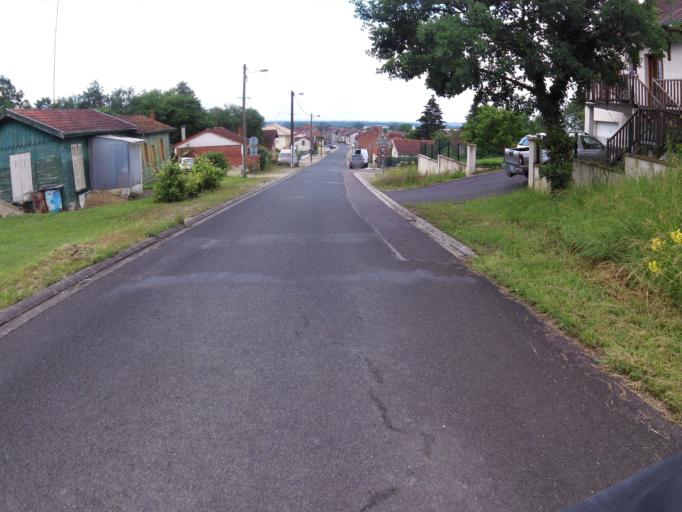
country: FR
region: Champagne-Ardenne
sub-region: Departement de la Marne
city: Sermaize-les-Bains
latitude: 48.7797
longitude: 4.9181
